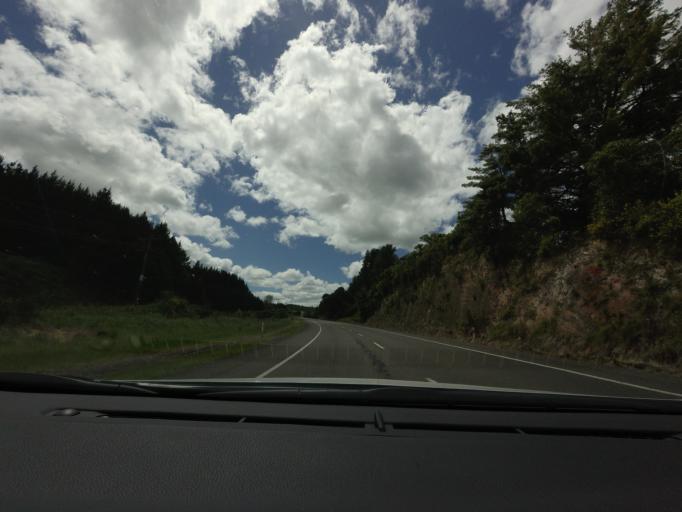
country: NZ
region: Bay of Plenty
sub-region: Rotorua District
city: Rotorua
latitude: -38.3288
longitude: 176.3693
